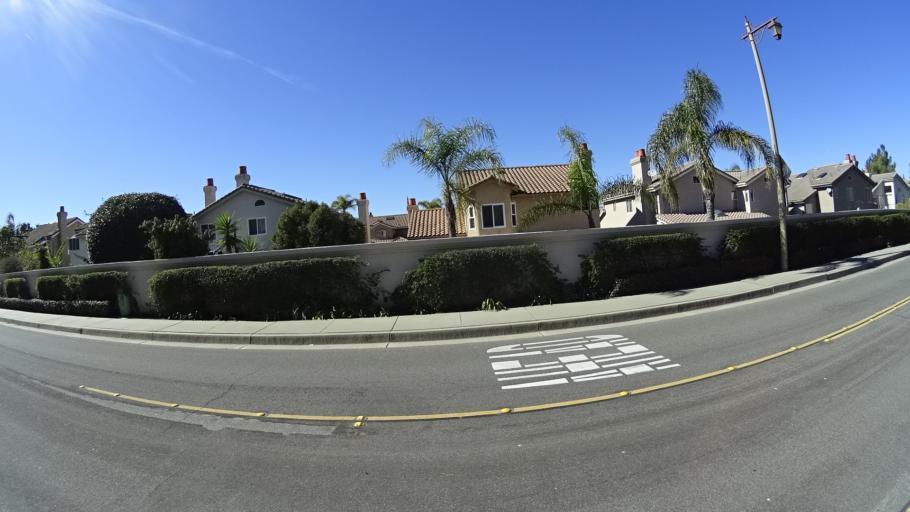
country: US
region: California
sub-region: Orange County
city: Villa Park
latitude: 33.8466
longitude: -117.7409
